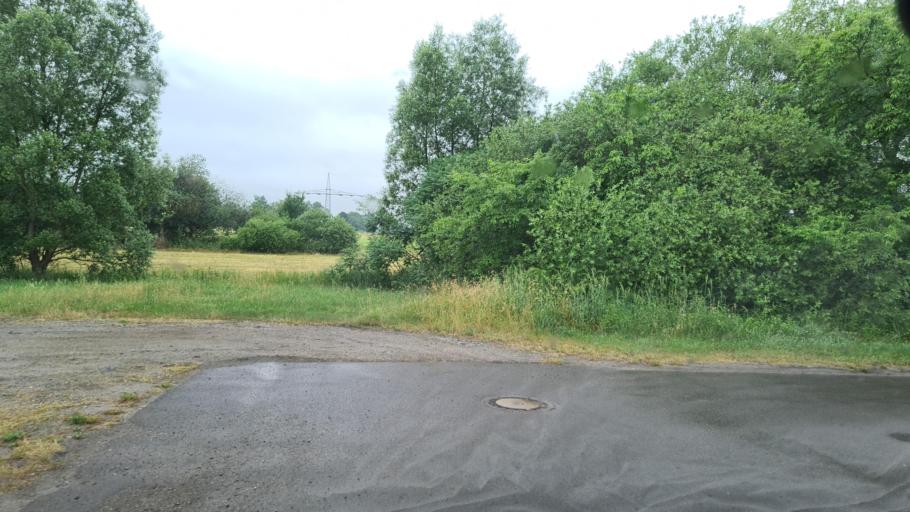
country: DE
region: Brandenburg
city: Lauchhammer
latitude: 51.4802
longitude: 13.7262
